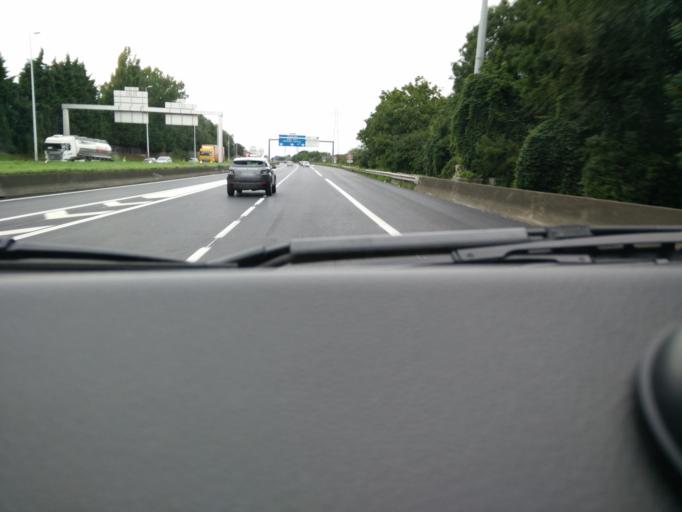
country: FR
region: Nord-Pas-de-Calais
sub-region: Departement du Nord
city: Wasquehal
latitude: 50.6711
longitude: 3.1148
